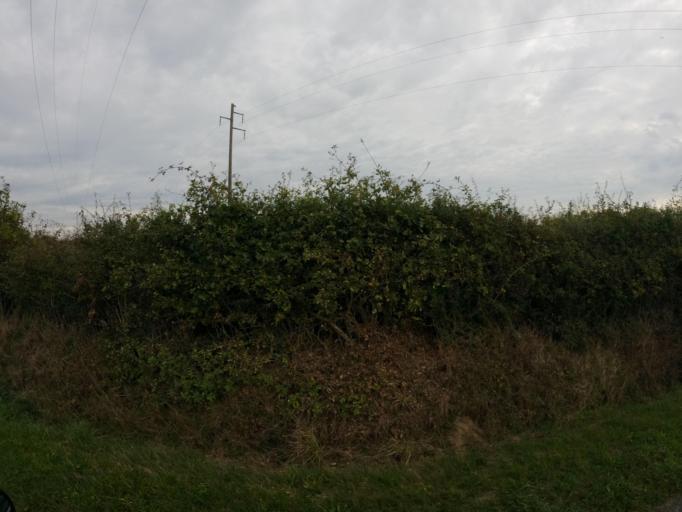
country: FR
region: Pays de la Loire
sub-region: Departement de Maine-et-Loire
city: Saint-Christophe-du-Bois
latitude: 47.0422
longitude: -0.9359
